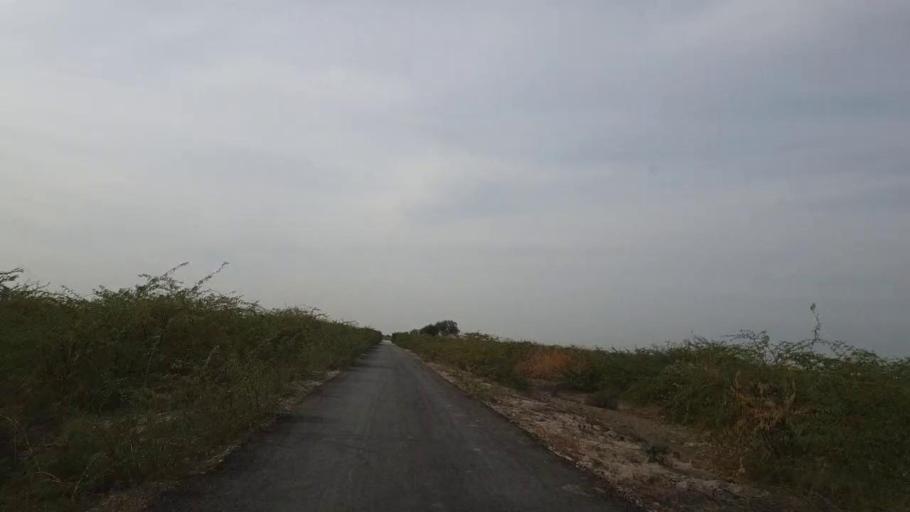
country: PK
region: Sindh
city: Nabisar
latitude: 24.9957
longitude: 69.5473
